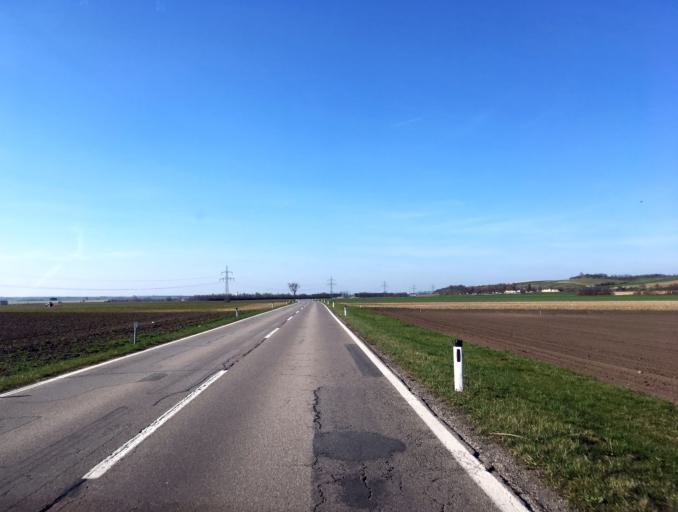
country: AT
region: Lower Austria
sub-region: Politischer Bezirk Bruck an der Leitha
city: Trautmannsdorf an der Leitha
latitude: 48.0497
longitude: 16.6194
